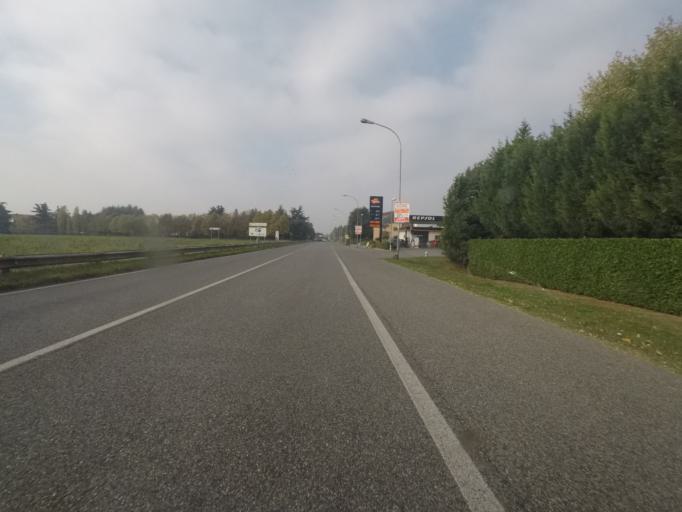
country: IT
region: Lombardy
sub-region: Provincia di Monza e Brianza
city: Concorezzo
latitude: 45.5987
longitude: 9.3520
